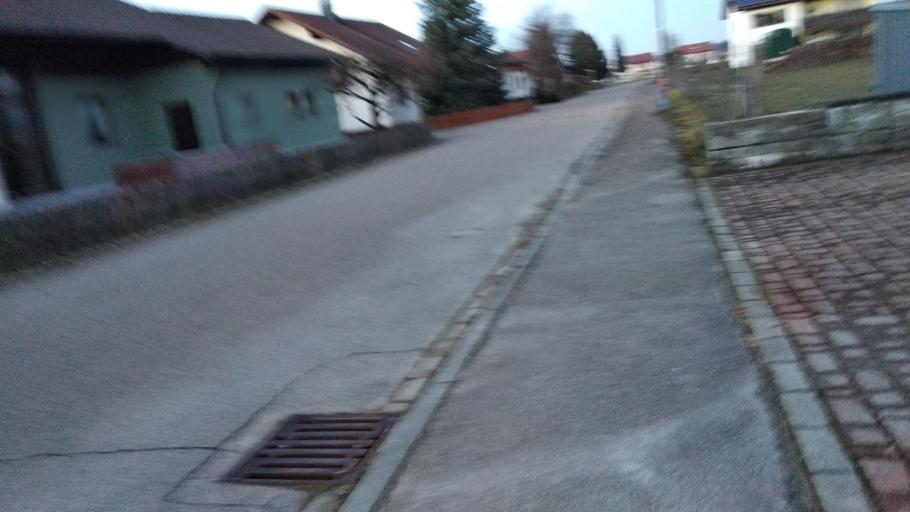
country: DE
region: Bavaria
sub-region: Swabia
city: Legau
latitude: 47.8555
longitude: 10.1256
